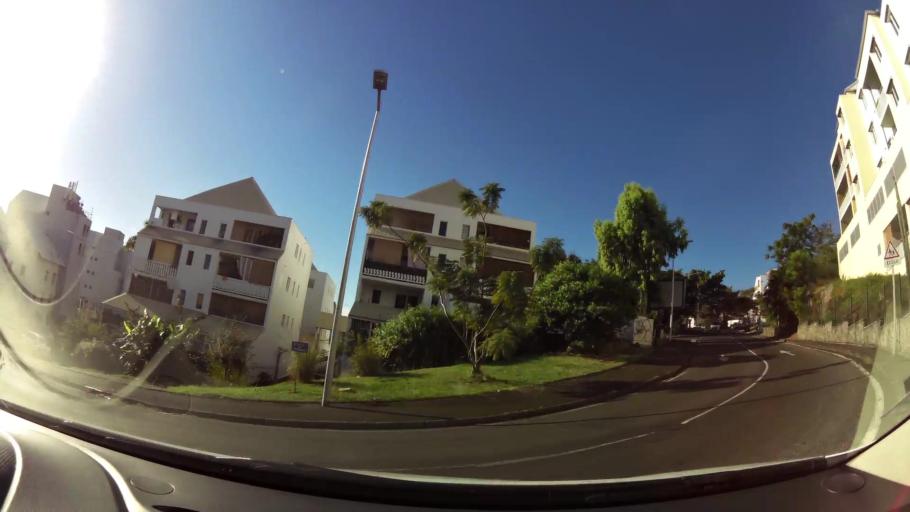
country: RE
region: Reunion
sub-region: Reunion
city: Saint-Denis
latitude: -20.8940
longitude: 55.4496
